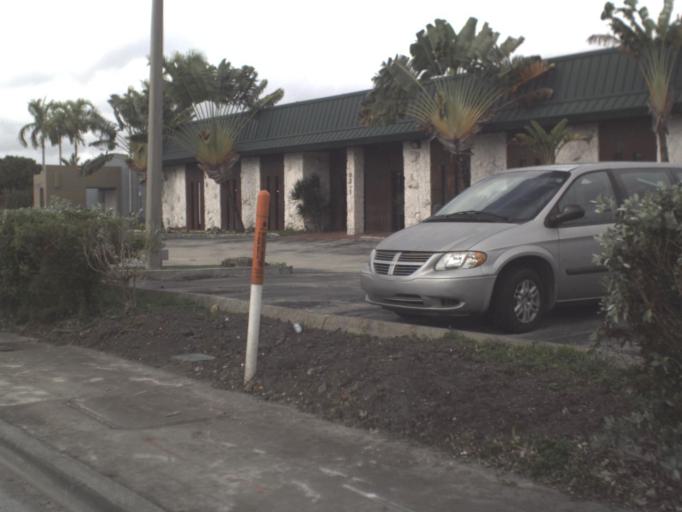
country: US
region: Florida
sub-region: Miami-Dade County
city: Doral
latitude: 25.8100
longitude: -80.3305
